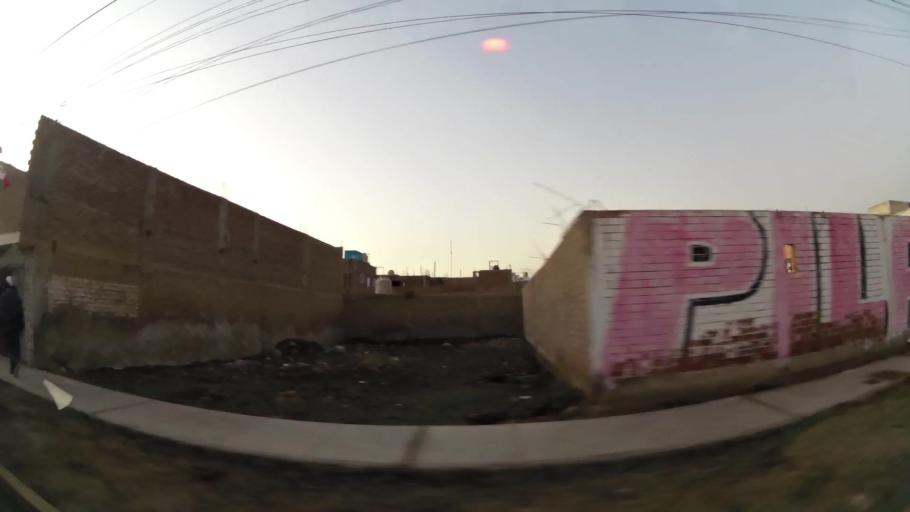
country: PE
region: Ica
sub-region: Provincia de Pisco
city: Pisco
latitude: -13.7069
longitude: -76.2069
